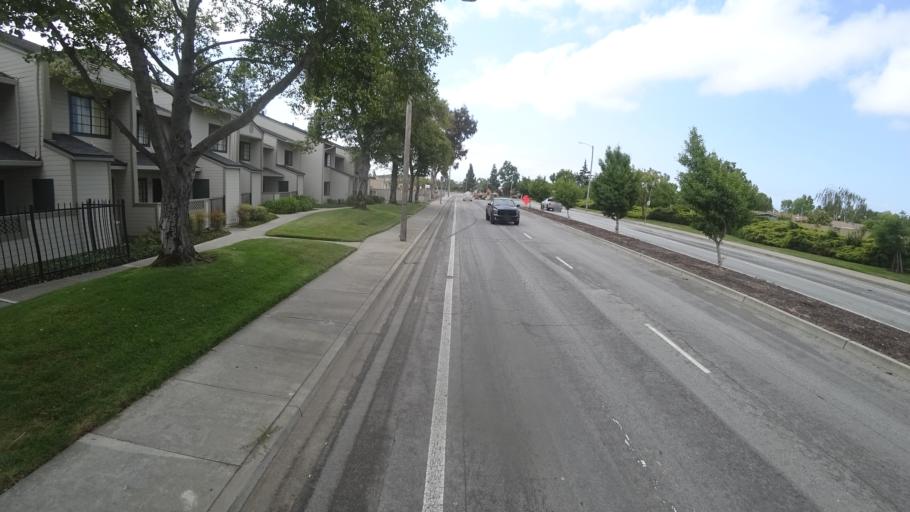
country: US
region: California
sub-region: Alameda County
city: Hayward
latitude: 37.6249
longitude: -122.0597
